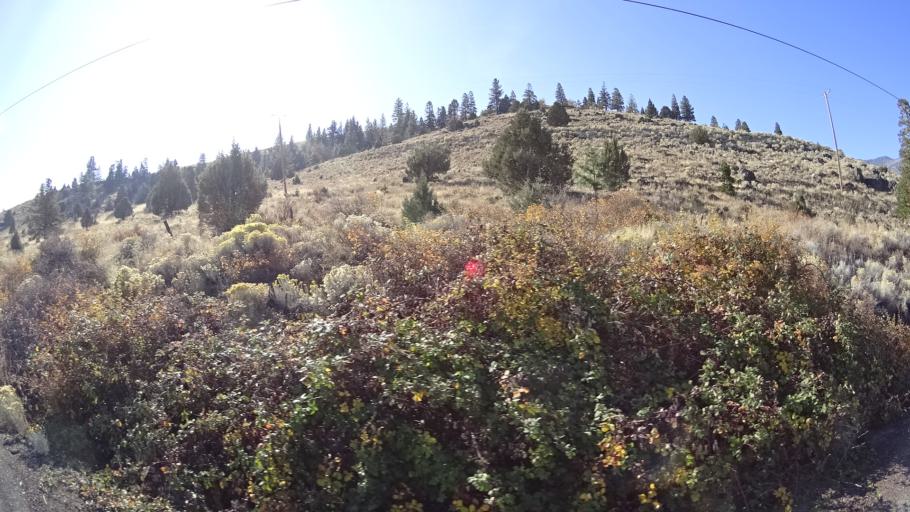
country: US
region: California
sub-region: Siskiyou County
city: Weed
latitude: 41.4684
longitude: -122.4712
